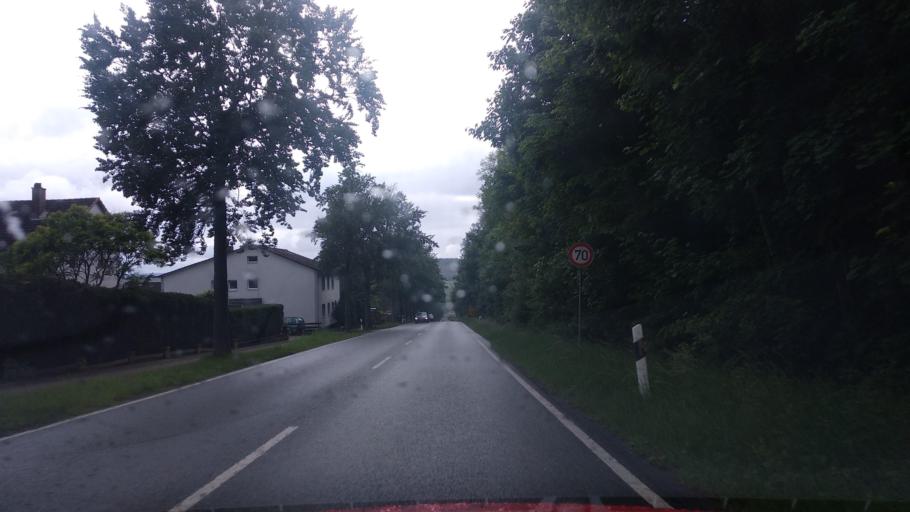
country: DE
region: Lower Saxony
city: Buchholz
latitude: 52.2378
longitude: 9.1351
